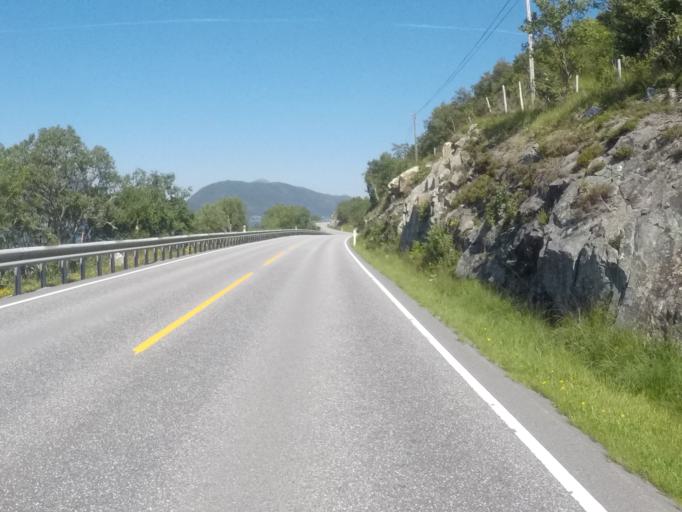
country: NO
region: More og Romsdal
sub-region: Hareid
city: Hareid
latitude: 62.2619
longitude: 5.9773
